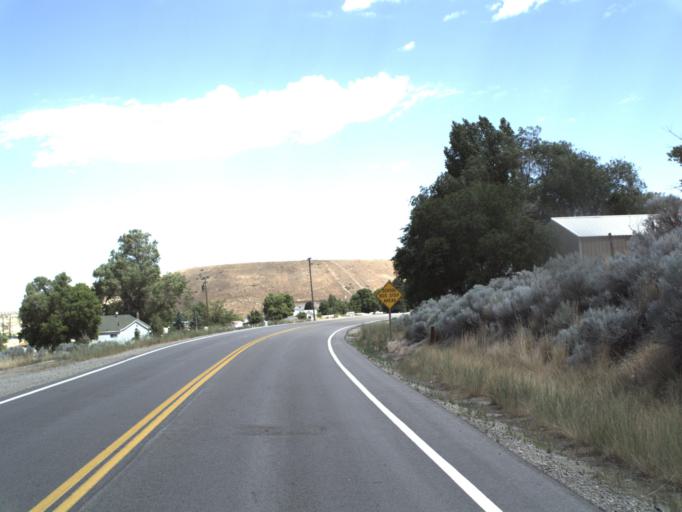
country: US
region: Utah
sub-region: Tooele County
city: Tooele
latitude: 40.4466
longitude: -112.3643
